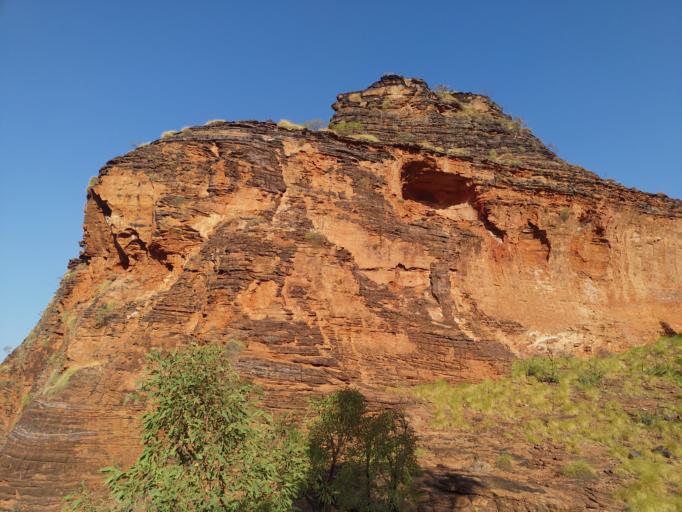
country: AU
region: Western Australia
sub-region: Wyndham-East Kimberley
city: Kununurra
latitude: -15.7622
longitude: 128.7512
